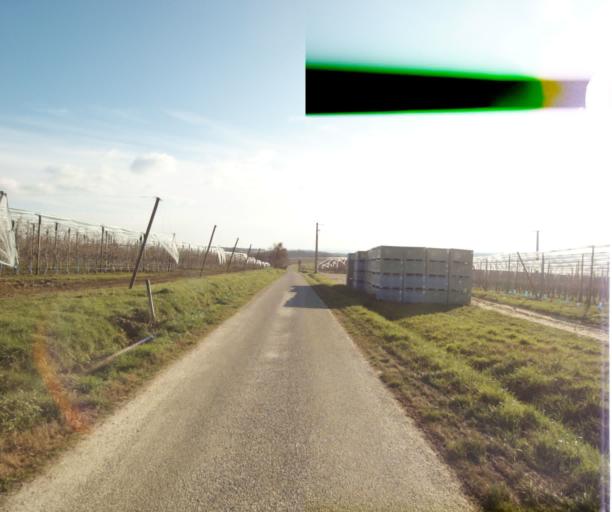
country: FR
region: Midi-Pyrenees
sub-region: Departement du Tarn-et-Garonne
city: Moissac
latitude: 44.1397
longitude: 1.0544
